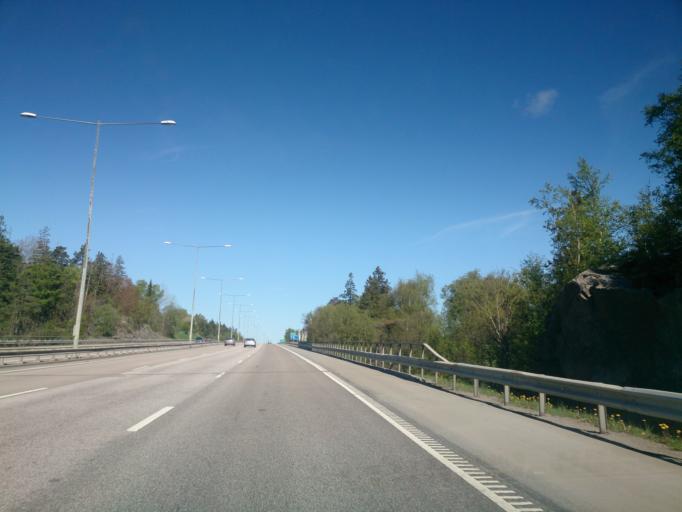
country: SE
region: Stockholm
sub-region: Haninge Kommun
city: Haninge
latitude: 59.1897
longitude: 18.1451
